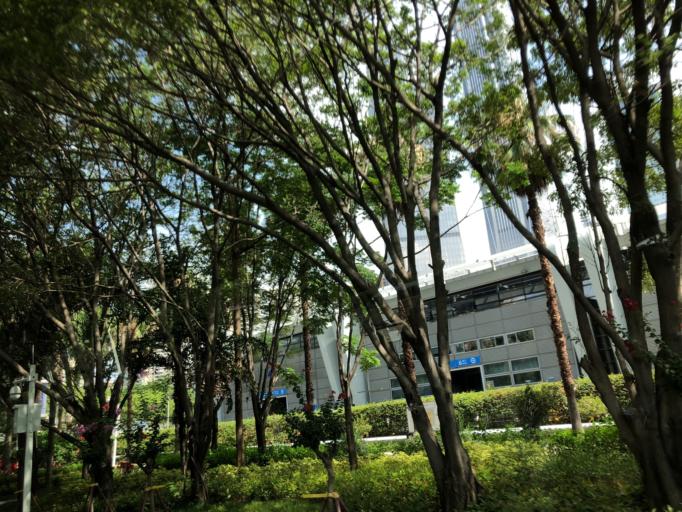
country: CN
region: Guangdong
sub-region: Shenzhen
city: Shenzhen
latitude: 22.5317
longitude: 114.0530
